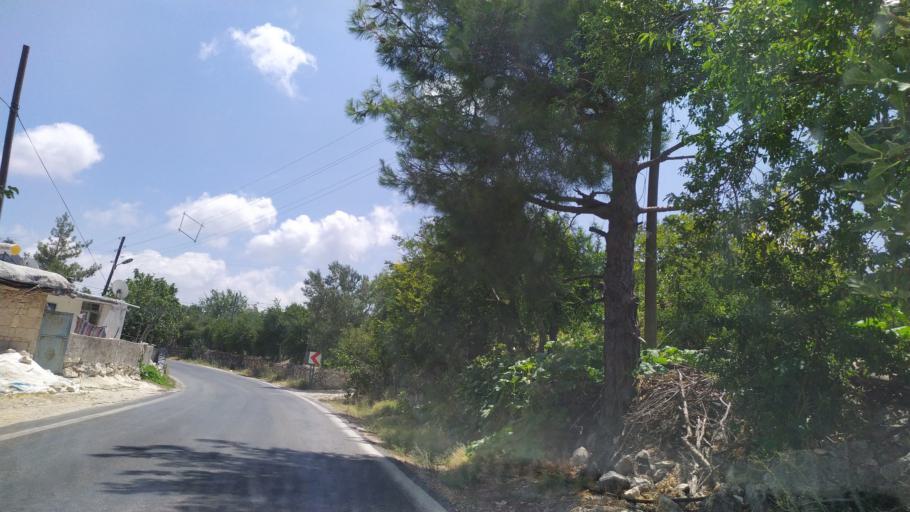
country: TR
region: Mersin
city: Gulnar
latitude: 36.2850
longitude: 33.3843
